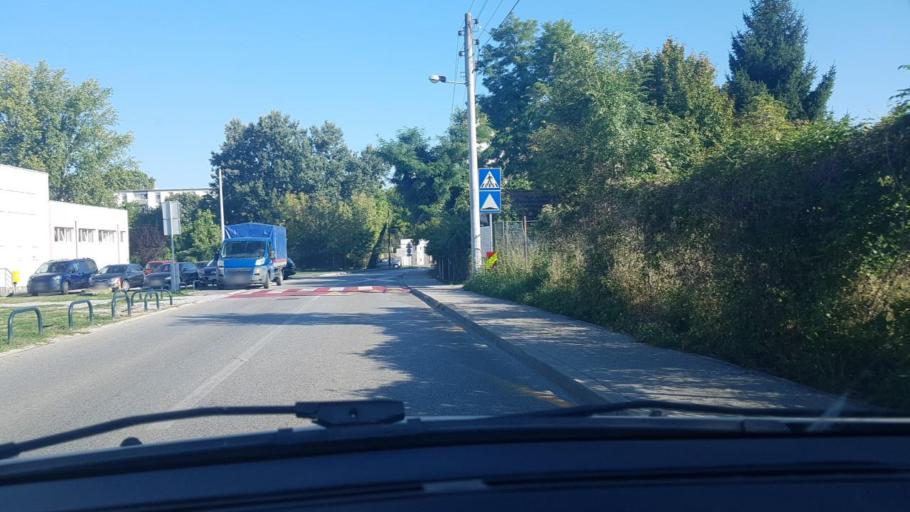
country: HR
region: Grad Zagreb
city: Novi Zagreb
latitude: 45.7710
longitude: 15.9704
